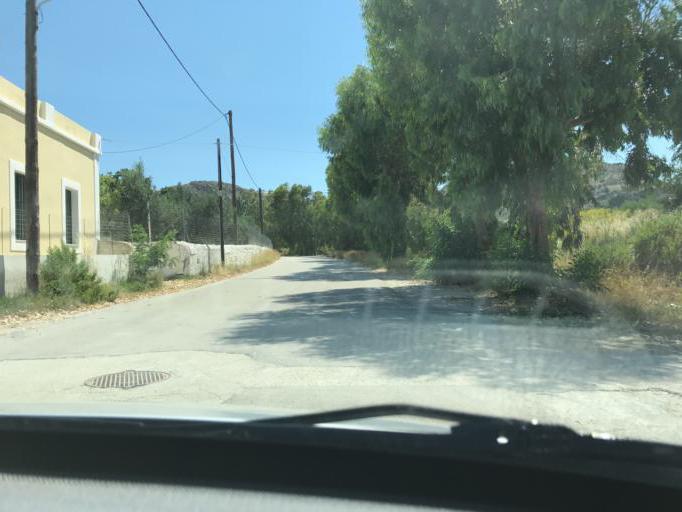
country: GR
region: South Aegean
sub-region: Nomos Dodekanisou
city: Karpathos
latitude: 35.5064
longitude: 27.2039
